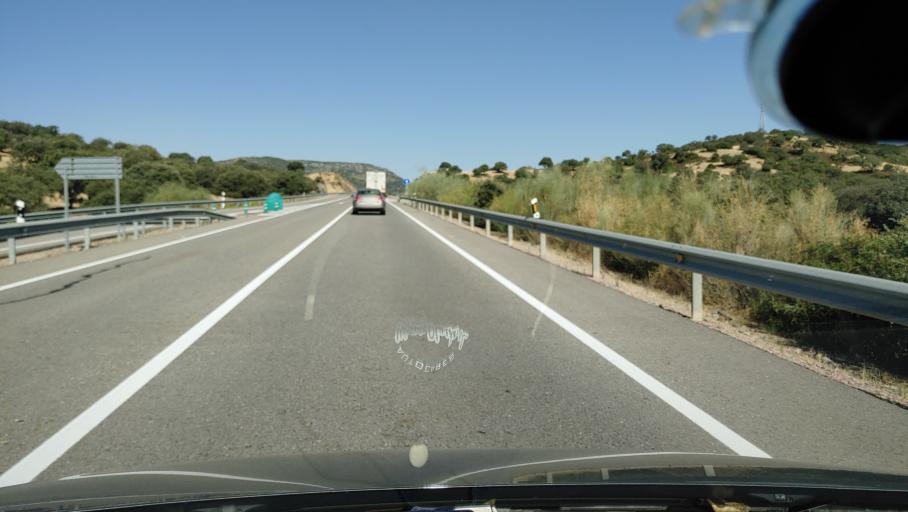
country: ES
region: Andalusia
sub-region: Province of Cordoba
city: Espiel
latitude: 38.1476
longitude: -4.9723
